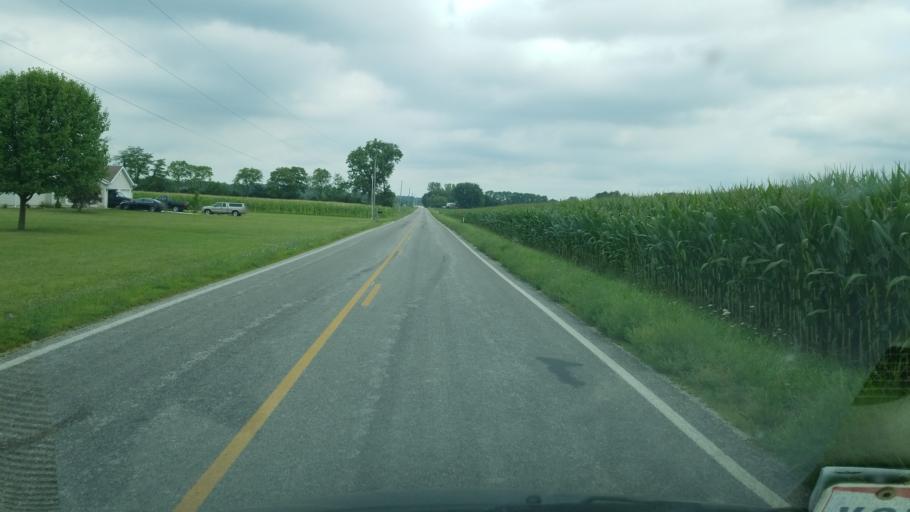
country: US
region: Ohio
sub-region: Seneca County
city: Tiffin
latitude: 41.1984
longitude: -83.1463
